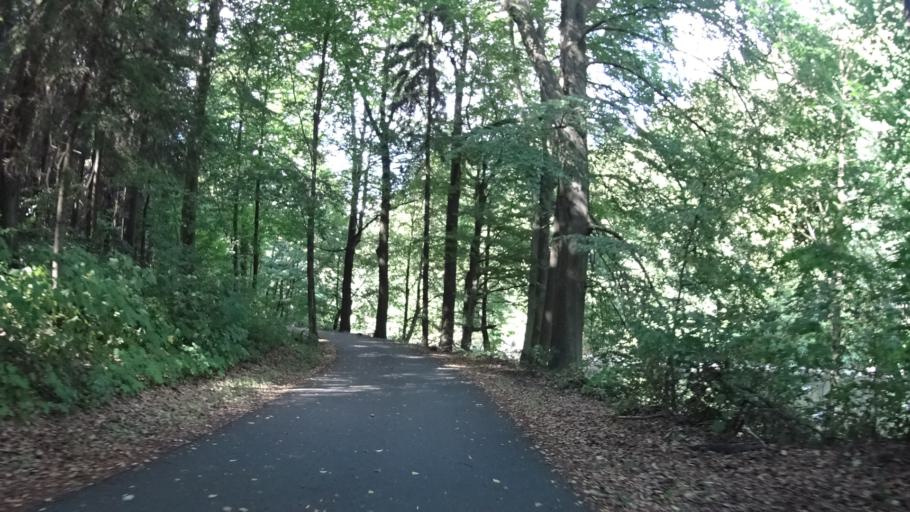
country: DE
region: Saxony
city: Ostritz
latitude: 50.9760
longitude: 14.9192
